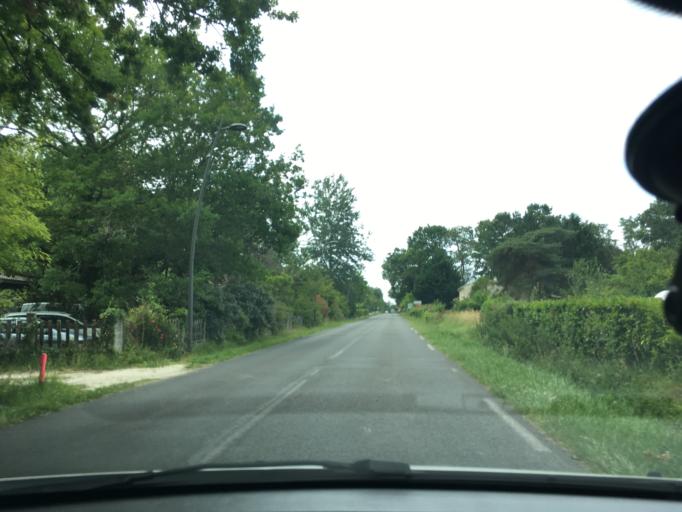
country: FR
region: Aquitaine
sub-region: Departement de la Gironde
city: Gaillan-en-Medoc
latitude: 45.3630
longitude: -1.0675
